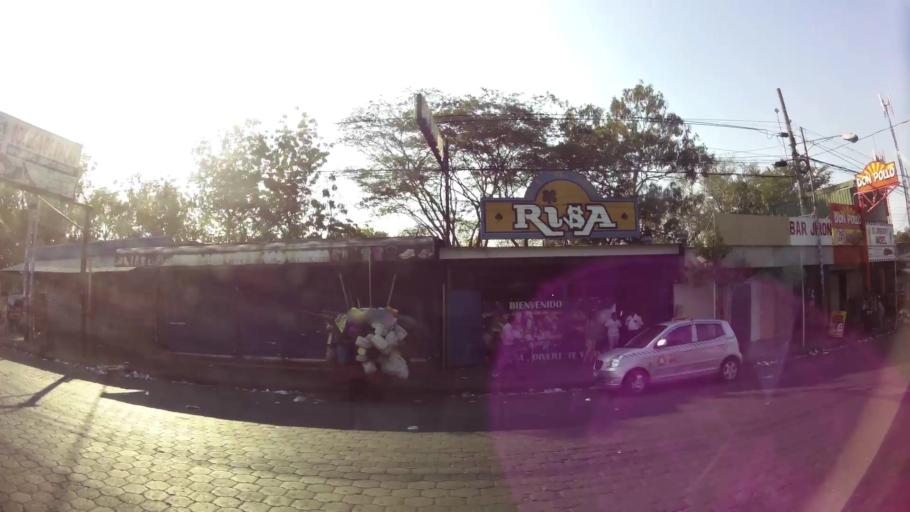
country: NI
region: Managua
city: Managua
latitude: 12.1446
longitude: -86.2613
